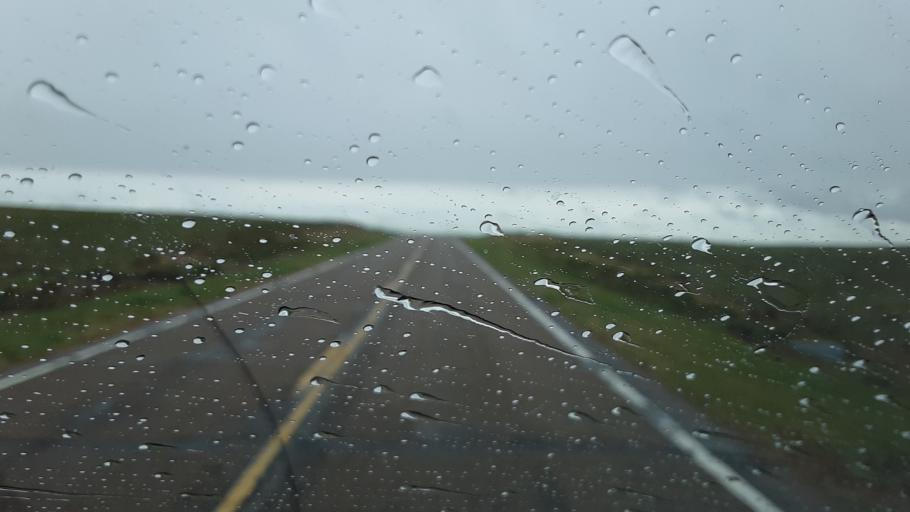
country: US
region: Colorado
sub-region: Lincoln County
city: Hugo
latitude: 38.8496
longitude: -103.2156
